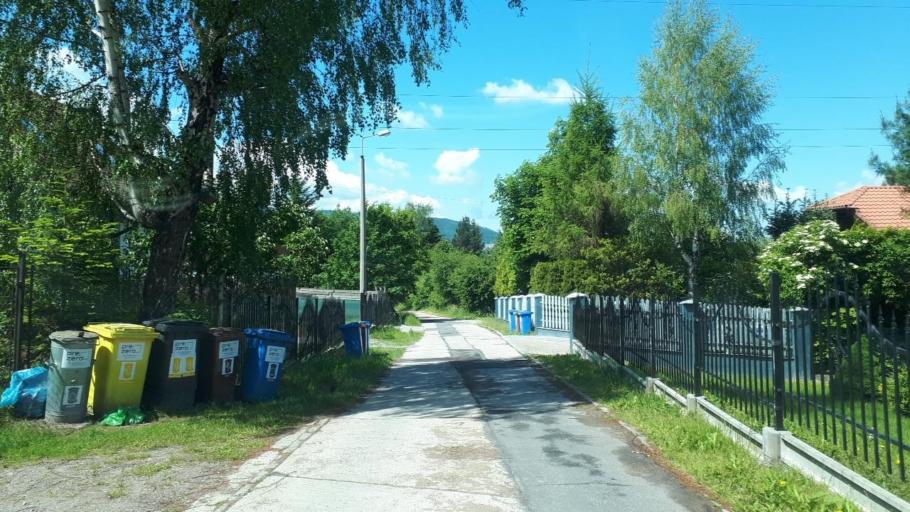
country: PL
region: Silesian Voivodeship
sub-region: Powiat bielski
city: Wilkowice
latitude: 49.7899
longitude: 19.0768
